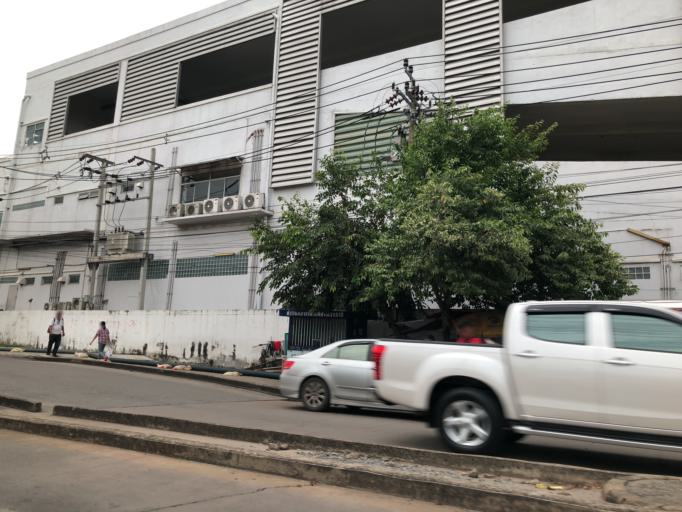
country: TH
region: Nonthaburi
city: Pak Kret
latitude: 13.9294
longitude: 100.5314
